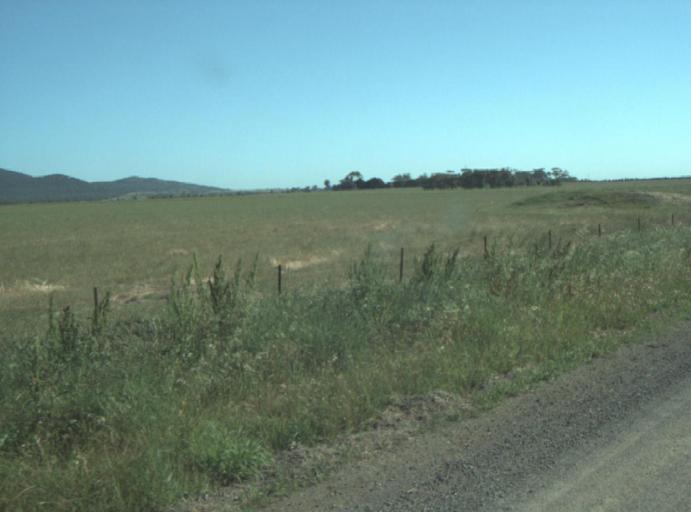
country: AU
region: Victoria
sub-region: Greater Geelong
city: Lara
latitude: -37.9957
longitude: 144.4483
